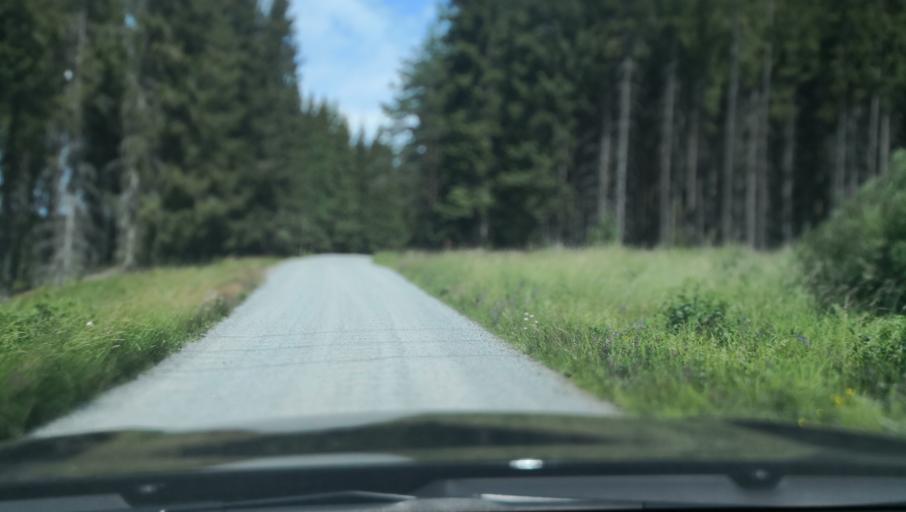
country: SE
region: Vaestmanland
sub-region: Surahammars Kommun
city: Ramnas
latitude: 59.8772
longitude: 16.0877
